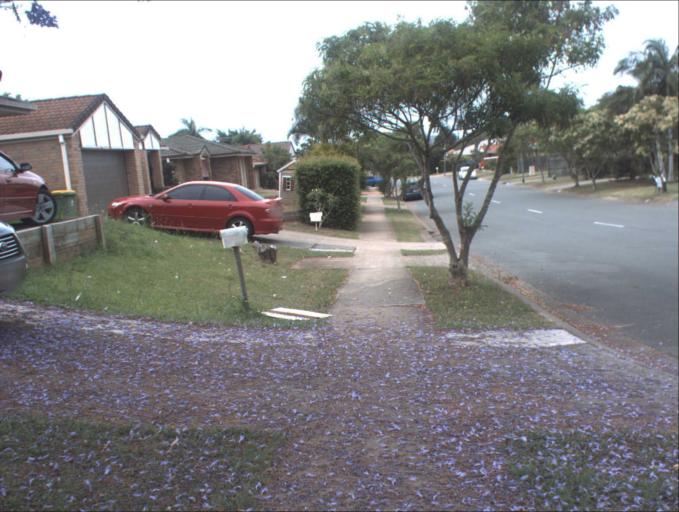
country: AU
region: Queensland
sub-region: Logan
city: Slacks Creek
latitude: -27.6755
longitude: 153.1679
